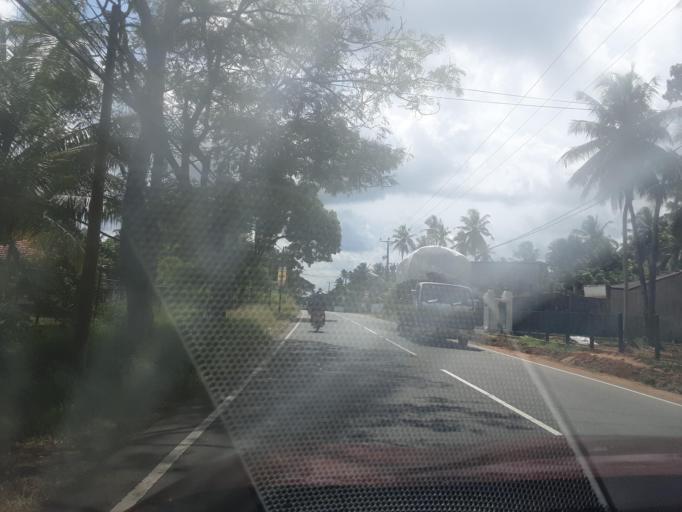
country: LK
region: North Western
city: Kuliyapitiya
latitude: 7.4756
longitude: 80.0105
